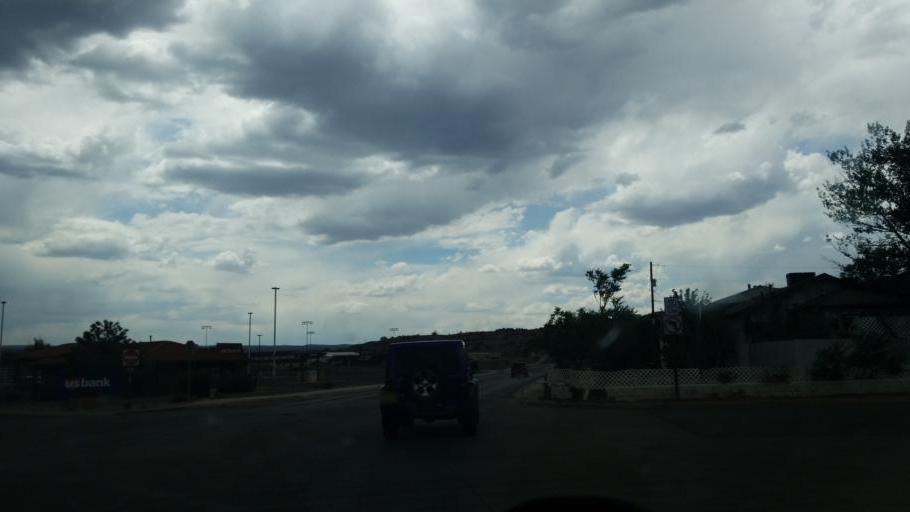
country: US
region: New Mexico
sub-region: Cibola County
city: Grants
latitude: 35.1612
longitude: -107.8411
